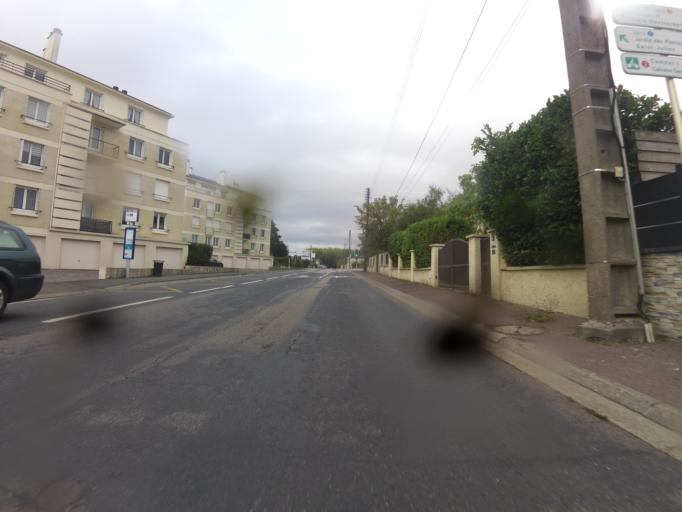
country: FR
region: Lower Normandy
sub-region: Departement du Calvados
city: Caen
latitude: 49.1944
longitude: -0.3704
